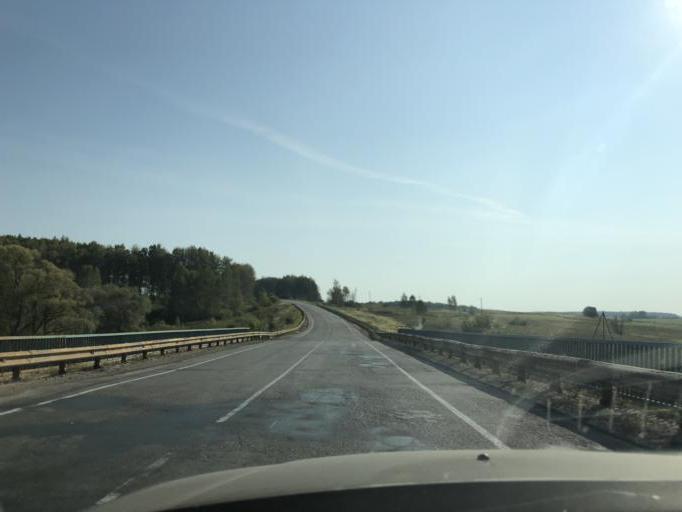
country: RU
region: Tula
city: Novogurovskiy
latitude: 54.4656
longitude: 37.4791
